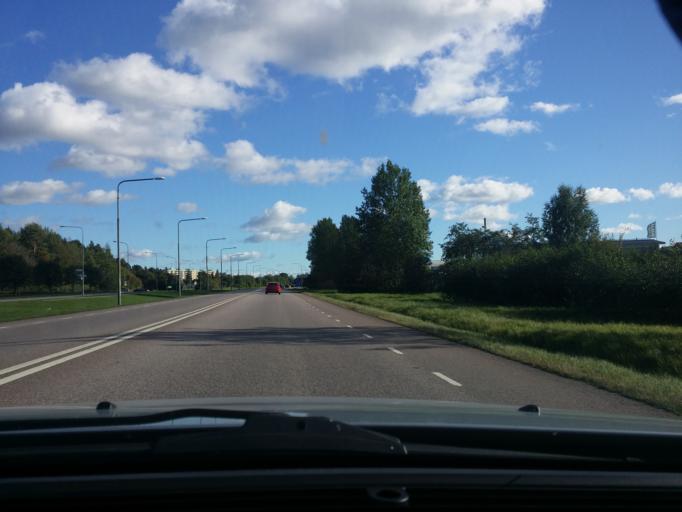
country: SE
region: Vaestmanland
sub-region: Vasteras
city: Vasteras
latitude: 59.6042
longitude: 16.4882
